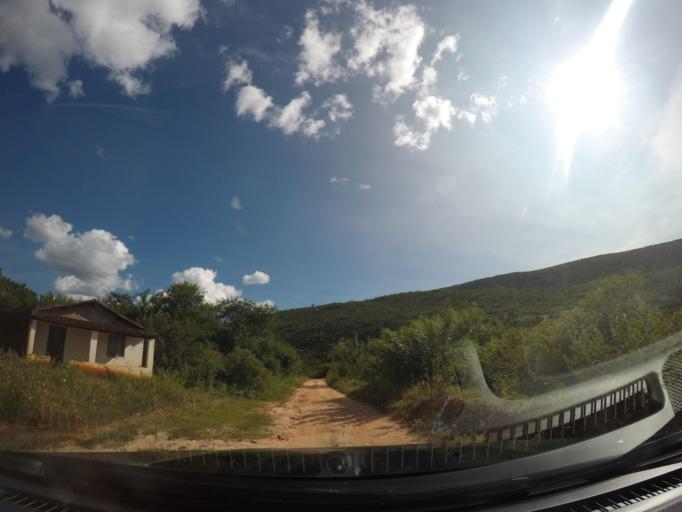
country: BR
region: Bahia
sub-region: Livramento Do Brumado
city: Livramento do Brumado
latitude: -13.2171
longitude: -41.6070
